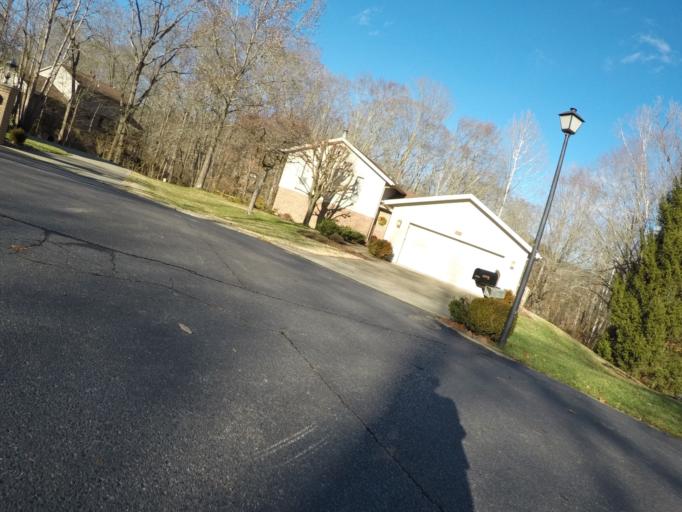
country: US
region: West Virginia
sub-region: Cabell County
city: Pea Ridge
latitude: 38.4208
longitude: -82.3257
